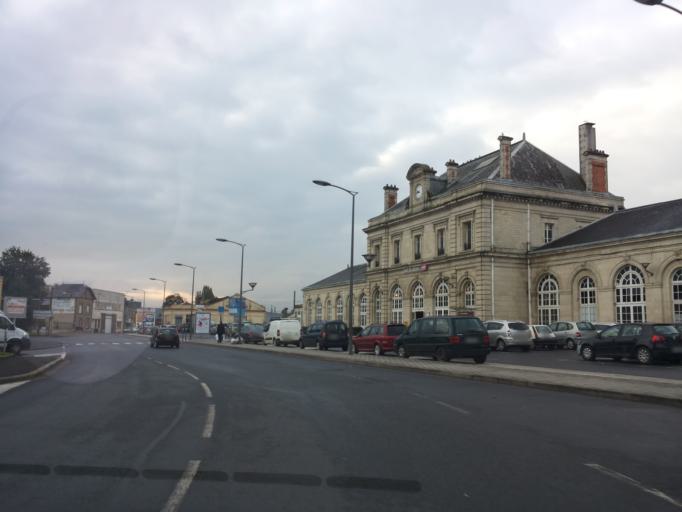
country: FR
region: Champagne-Ardenne
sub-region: Departement des Ardennes
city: Sedan
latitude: 49.6960
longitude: 4.9299
